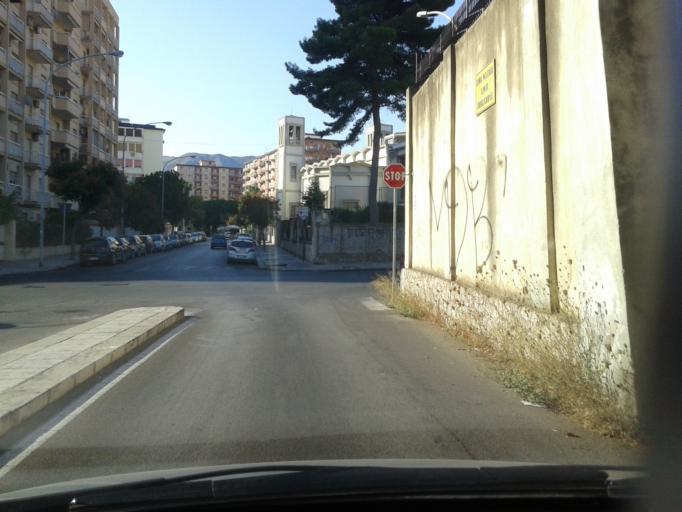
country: IT
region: Sicily
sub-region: Palermo
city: Palermo
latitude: 38.1028
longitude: 13.3341
